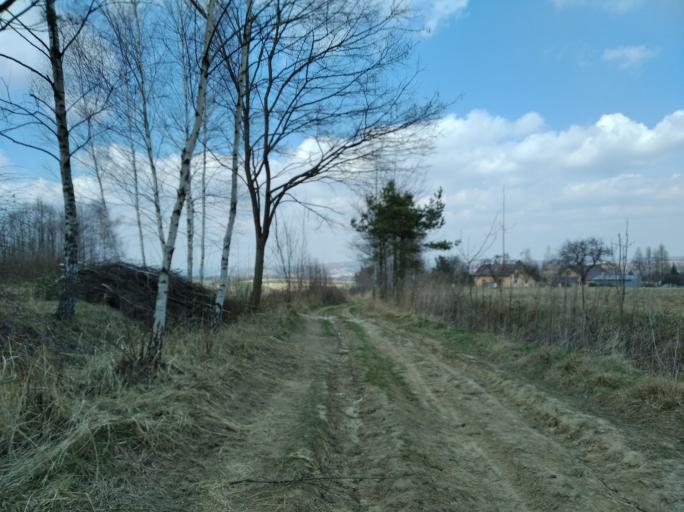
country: PL
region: Subcarpathian Voivodeship
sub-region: Powiat strzyzowski
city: Strzyzow
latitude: 49.8315
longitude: 21.8068
